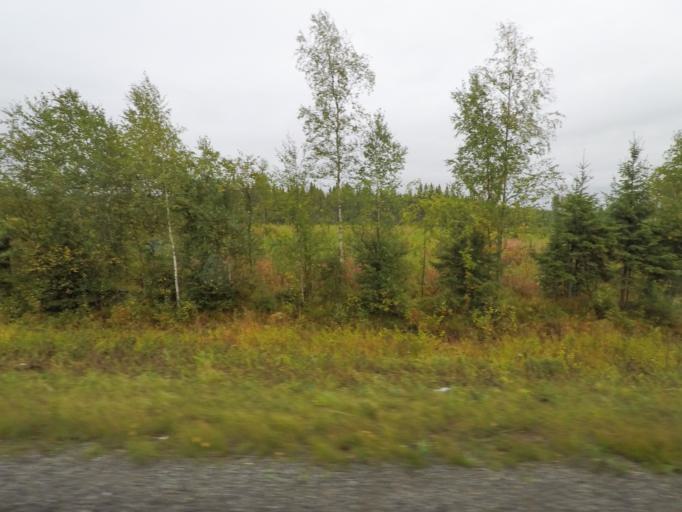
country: FI
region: Southern Savonia
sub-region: Pieksaemaeki
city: Joroinen
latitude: 62.0612
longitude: 27.8095
